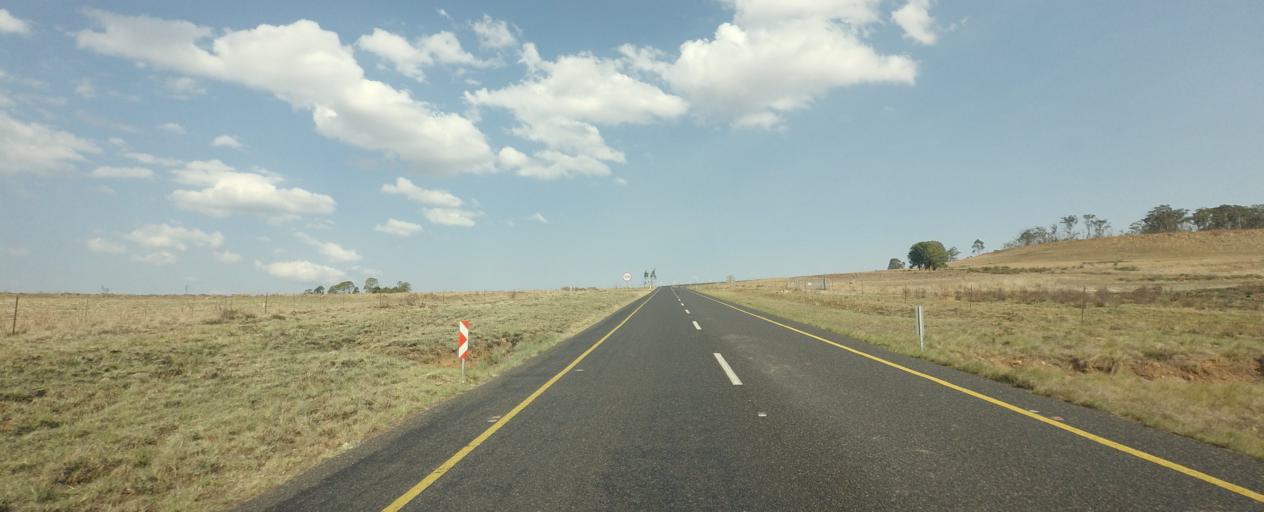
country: ZA
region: Mpumalanga
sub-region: Ehlanzeni District
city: Lydenburg
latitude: -25.1059
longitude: 30.5742
